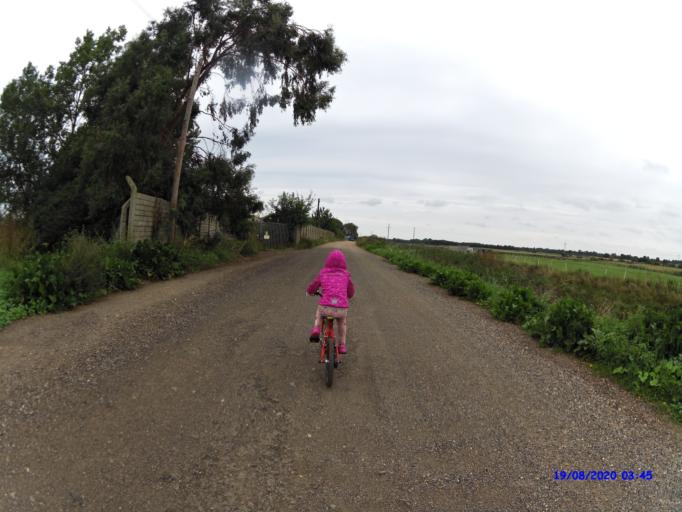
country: GB
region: England
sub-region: Cambridgeshire
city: Ramsey
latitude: 52.4577
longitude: -0.1107
